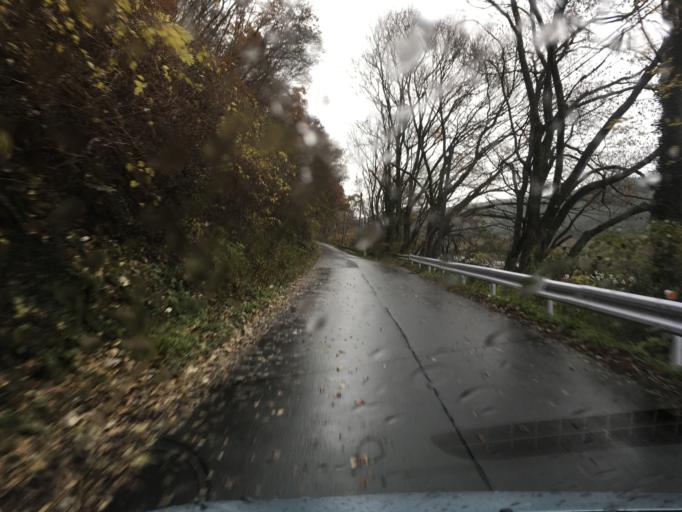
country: JP
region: Iwate
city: Ichinoseki
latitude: 38.8162
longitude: 141.2534
